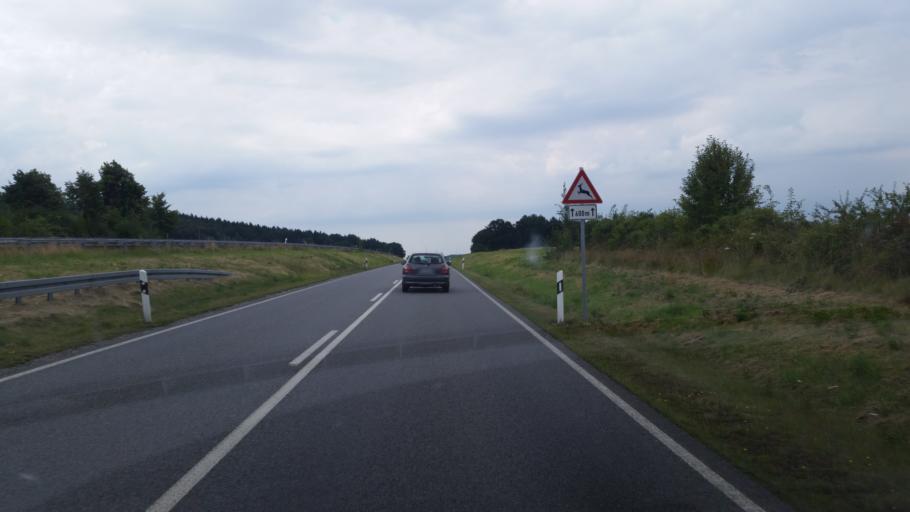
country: DE
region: Saxony
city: Elstra
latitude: 51.2115
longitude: 14.1527
